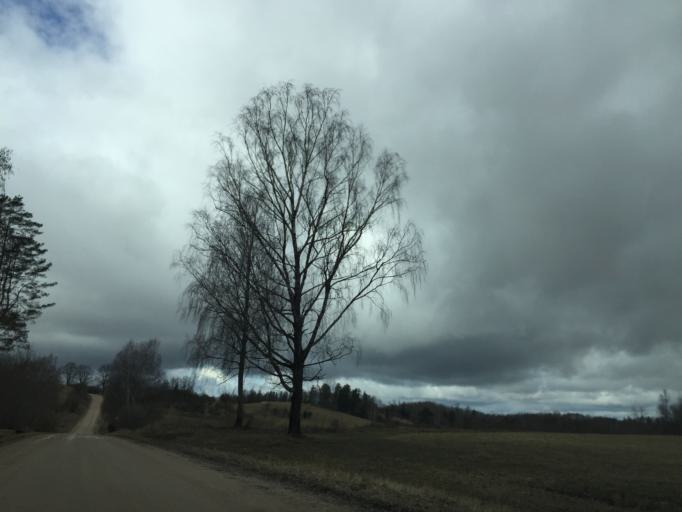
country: LV
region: Ilukste
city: Ilukste
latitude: 56.0662
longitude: 26.0941
